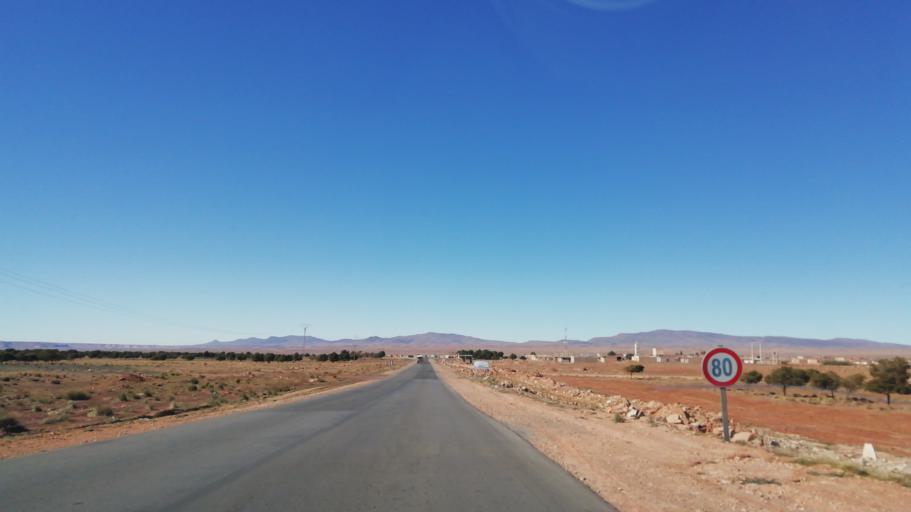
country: DZ
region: El Bayadh
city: El Bayadh
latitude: 33.6317
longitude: 1.3602
